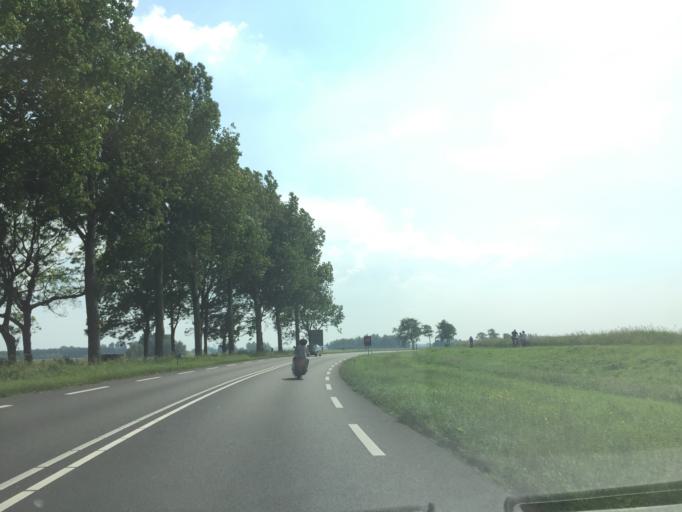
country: NL
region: South Holland
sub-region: Gemeente Leiden
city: Leiden
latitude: 52.1115
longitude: 4.4955
